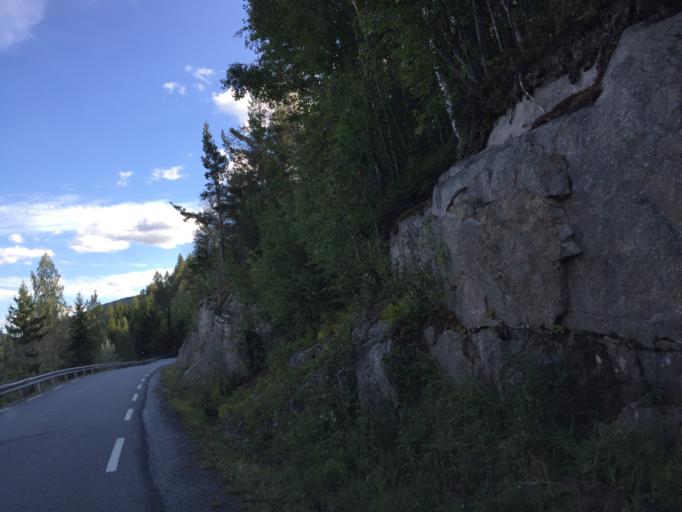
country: NO
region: Buskerud
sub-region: Ovre Eiker
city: Hokksund
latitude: 59.6533
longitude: 9.9144
